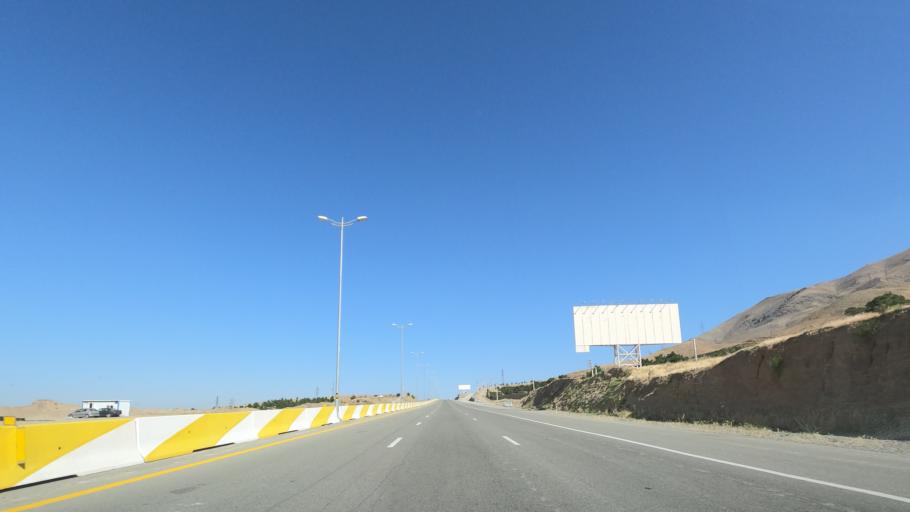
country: IR
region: Tehran
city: Shahr-e Qods
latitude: 35.7630
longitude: 51.0724
